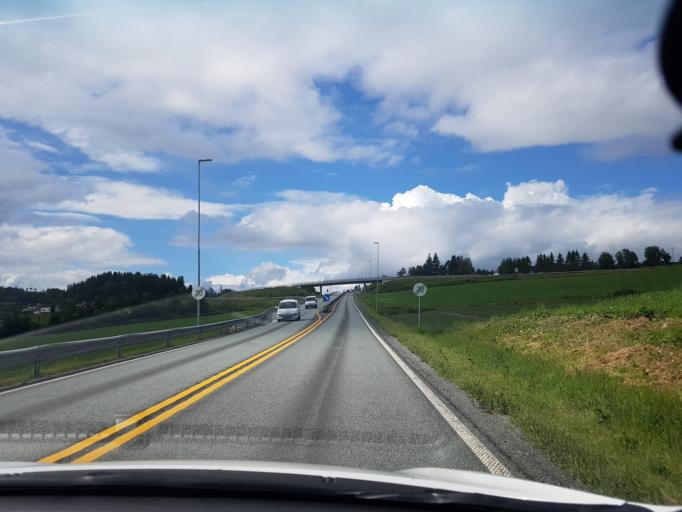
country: NO
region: Nord-Trondelag
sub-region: Stjordal
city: Stjordal
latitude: 63.5263
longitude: 10.8417
